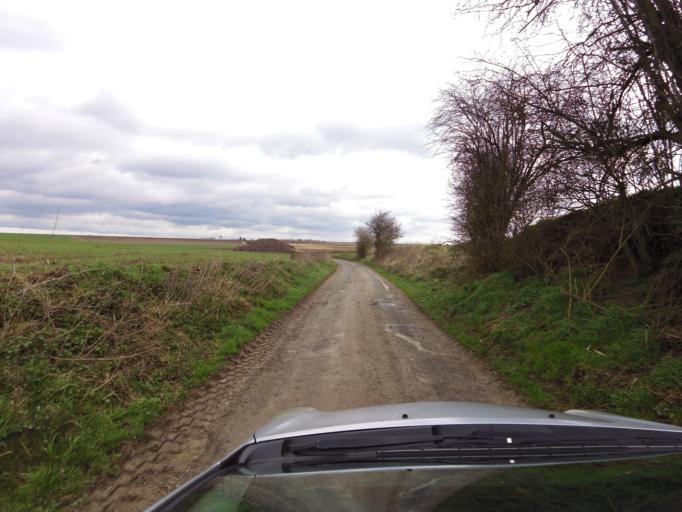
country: FR
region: Nord-Pas-de-Calais
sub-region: Departement du Pas-de-Calais
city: Beaurains
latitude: 50.2183
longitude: 2.7900
